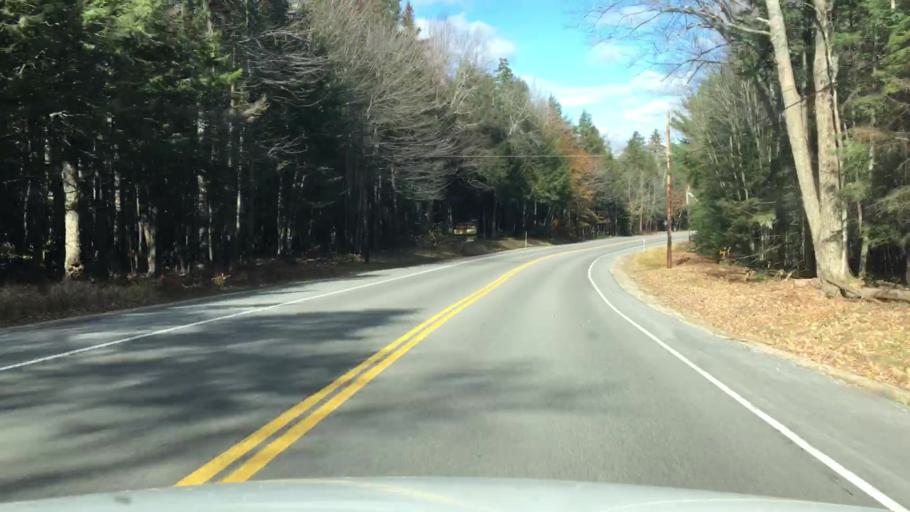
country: US
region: New Hampshire
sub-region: Coos County
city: Gorham
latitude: 44.3475
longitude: -71.1954
